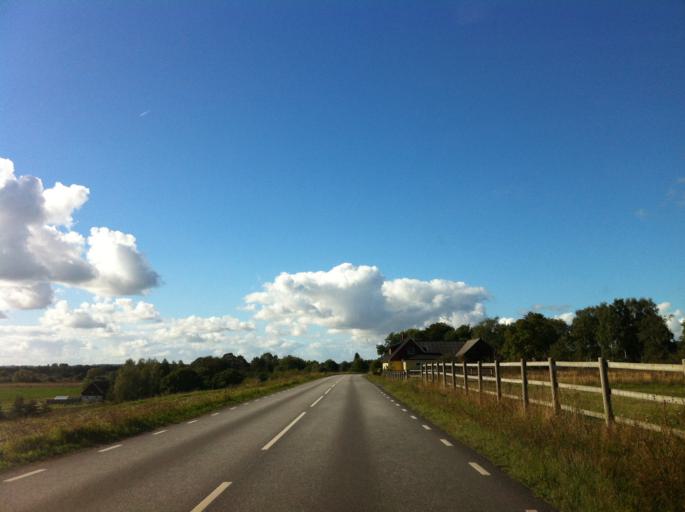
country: SE
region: Skane
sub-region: Hoors Kommun
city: Loberod
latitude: 55.7277
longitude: 13.4871
